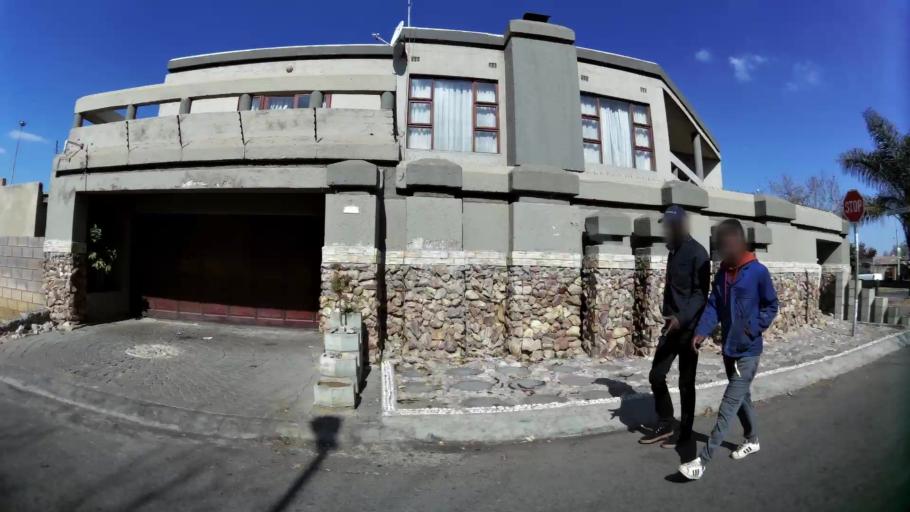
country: ZA
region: Gauteng
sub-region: City of Johannesburg Metropolitan Municipality
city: Soweto
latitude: -26.2531
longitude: 27.8855
